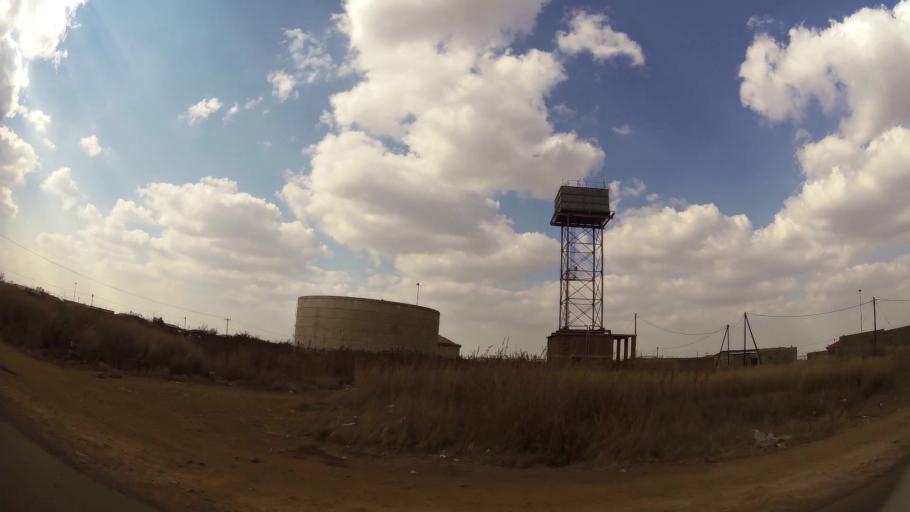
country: ZA
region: Mpumalanga
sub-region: Nkangala District Municipality
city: Delmas
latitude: -26.0985
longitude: 28.6779
